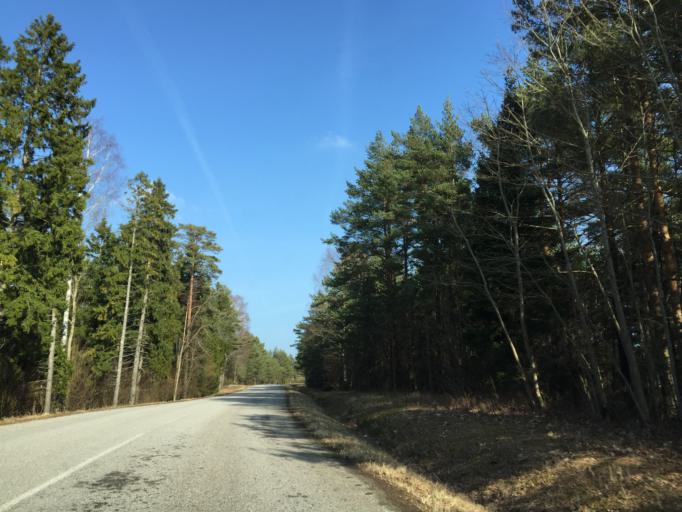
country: EE
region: Saare
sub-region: Kuressaare linn
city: Kuressaare
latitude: 58.0448
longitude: 22.1150
